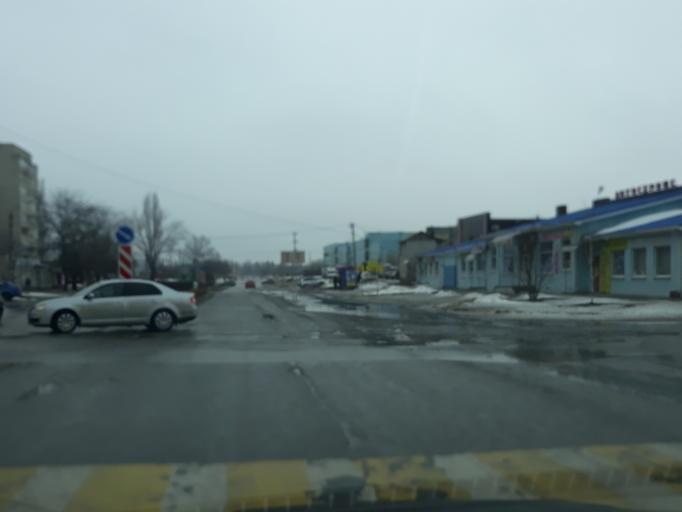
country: RU
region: Rostov
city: Novobessergenovka
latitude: 47.2174
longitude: 38.8625
